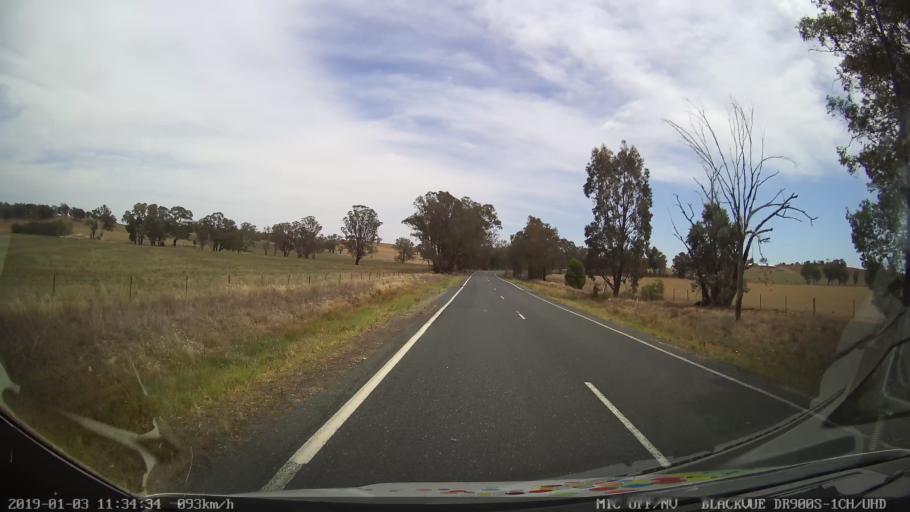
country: AU
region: New South Wales
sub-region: Weddin
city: Grenfell
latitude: -33.9333
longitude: 148.1623
